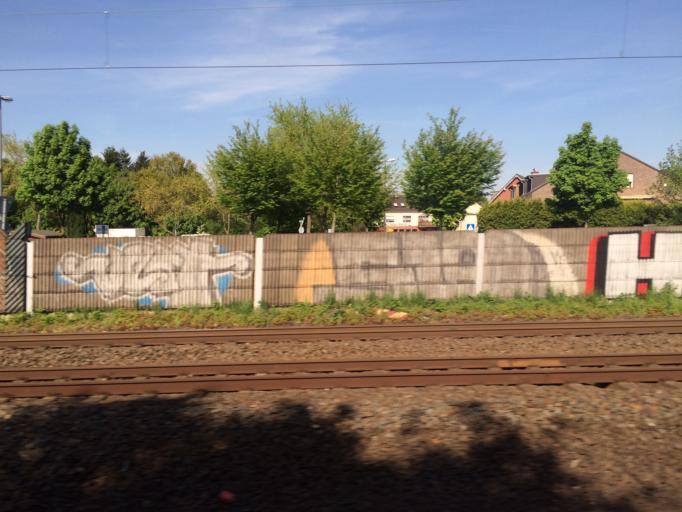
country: DE
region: North Rhine-Westphalia
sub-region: Regierungsbezirk Koln
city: Muelheim
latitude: 50.9846
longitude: 7.0043
